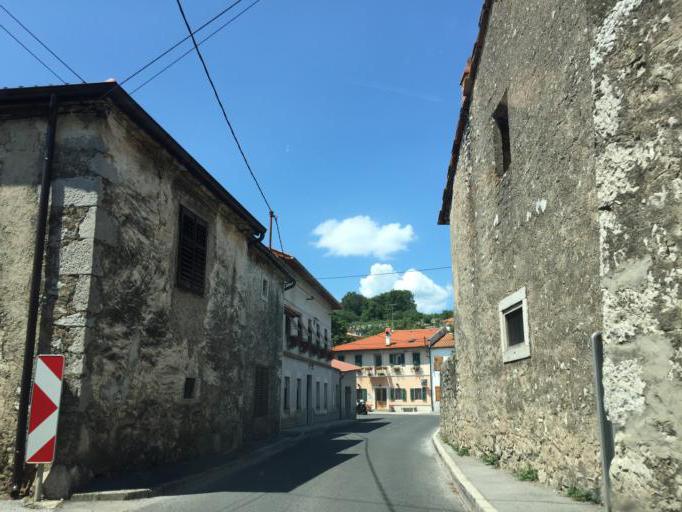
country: SI
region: Sezana
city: Sezana
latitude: 45.7544
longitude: 13.8558
